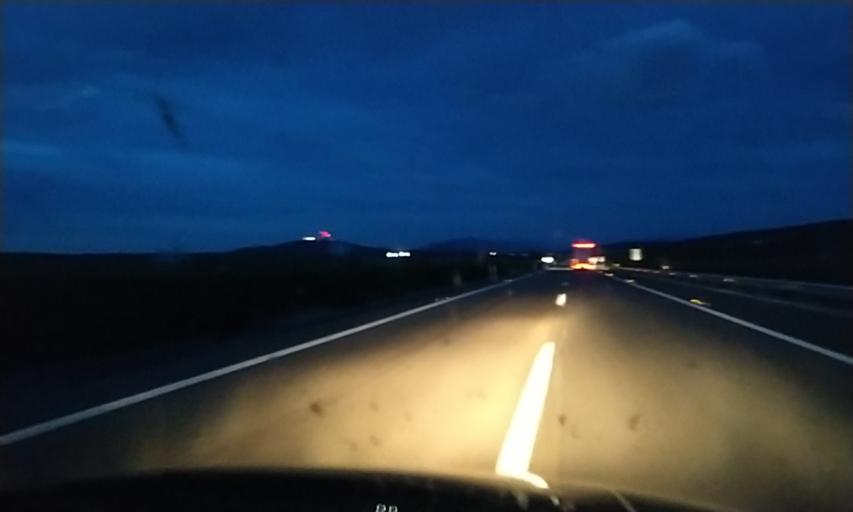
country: ES
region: Extremadura
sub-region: Provincia de Caceres
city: Galisteo
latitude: 39.9414
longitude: -6.2019
